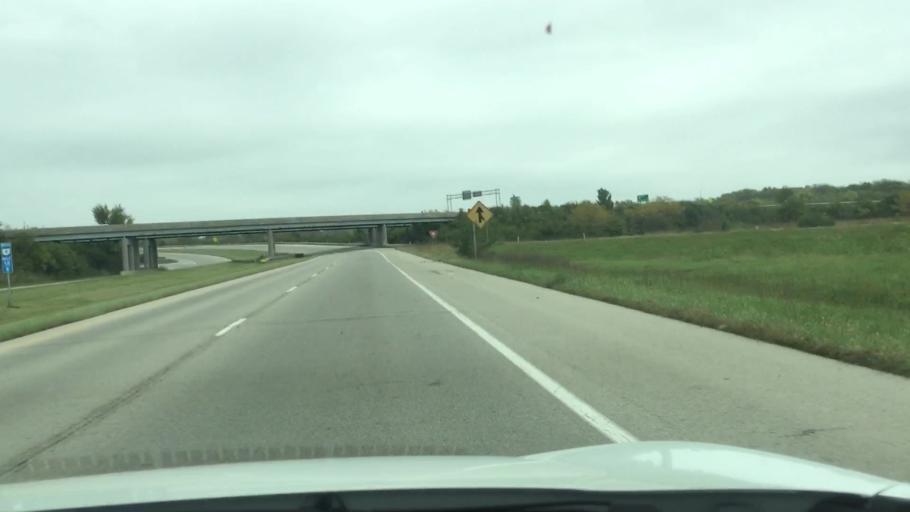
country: US
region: Ohio
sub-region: Montgomery County
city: Riverside
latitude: 39.7998
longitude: -84.1034
